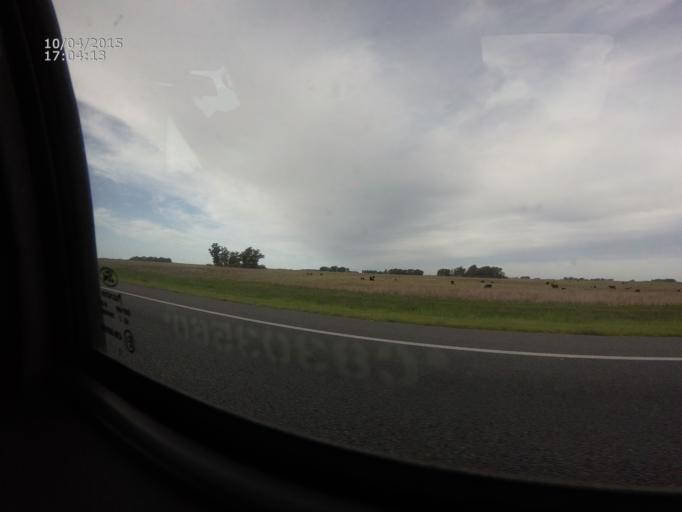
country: AR
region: Buenos Aires
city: Coronel Vidal
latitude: -37.4047
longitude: -57.7414
